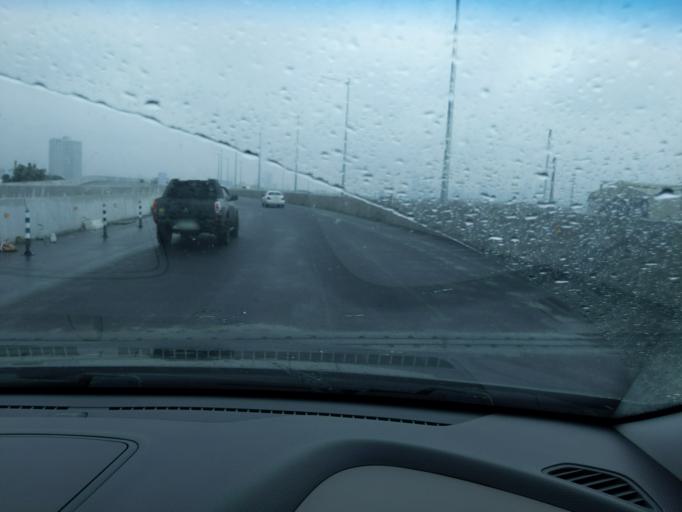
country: PH
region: Metro Manila
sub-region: San Juan
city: San Juan
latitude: 14.5890
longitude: 121.0126
